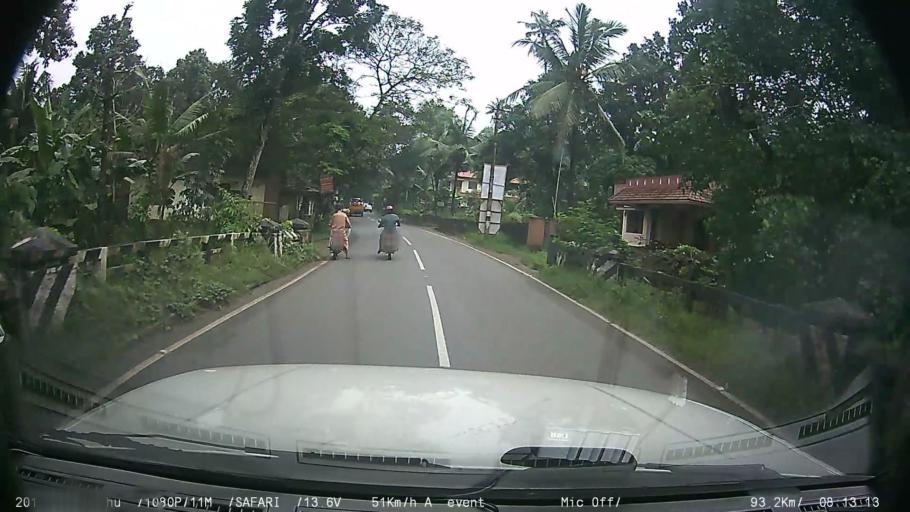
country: IN
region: Kerala
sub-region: Kottayam
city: Kottayam
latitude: 9.6142
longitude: 76.6045
